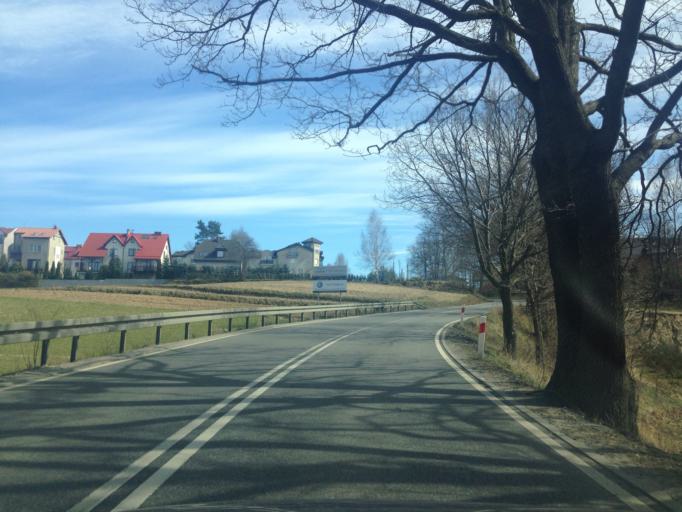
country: PL
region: Pomeranian Voivodeship
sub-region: Gdynia
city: Wielki Kack
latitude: 54.4762
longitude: 18.4607
